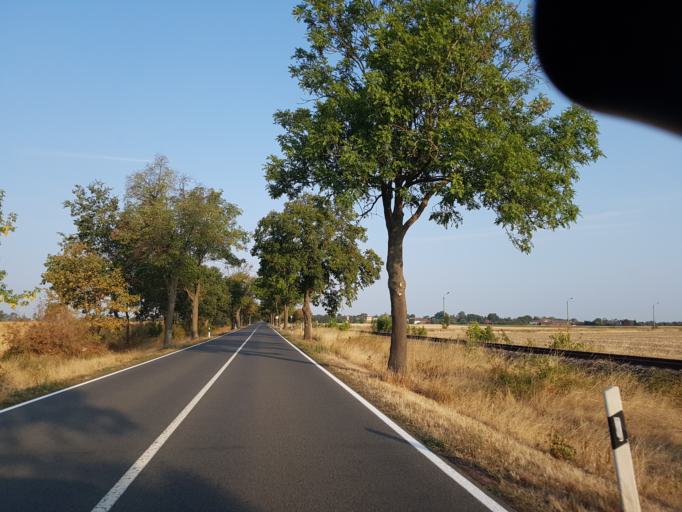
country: DE
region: Saxony-Anhalt
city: Kemberg
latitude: 51.7967
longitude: 12.6985
